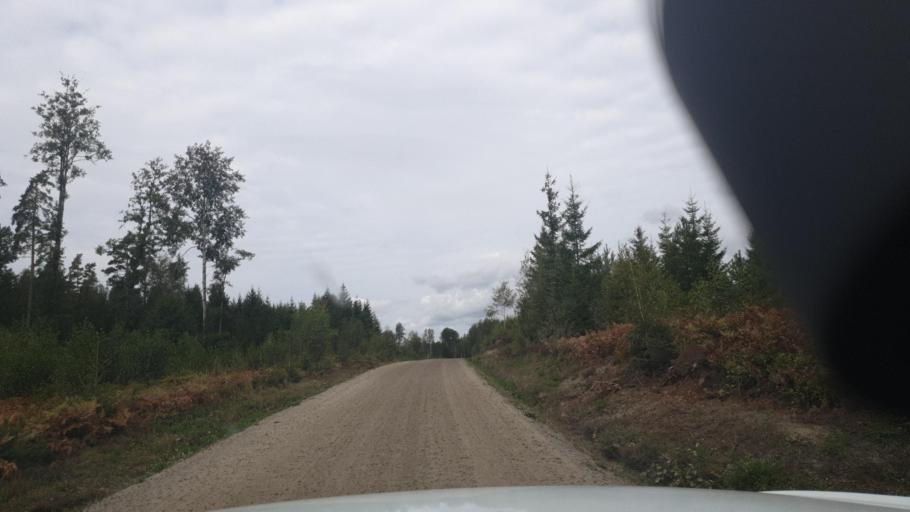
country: SE
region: Vaermland
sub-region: Karlstads Kommun
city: Edsvalla
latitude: 59.5197
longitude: 13.0070
